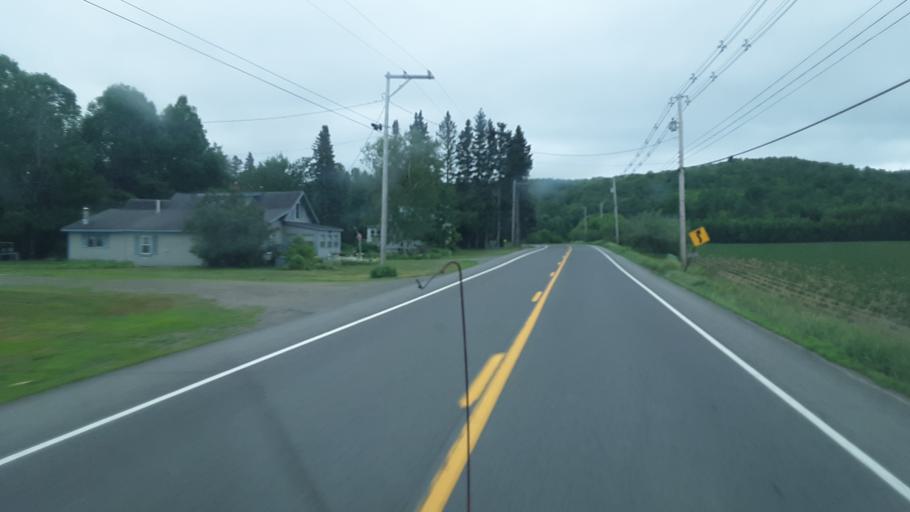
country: US
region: Maine
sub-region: Penobscot County
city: Patten
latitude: 45.8908
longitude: -68.4239
